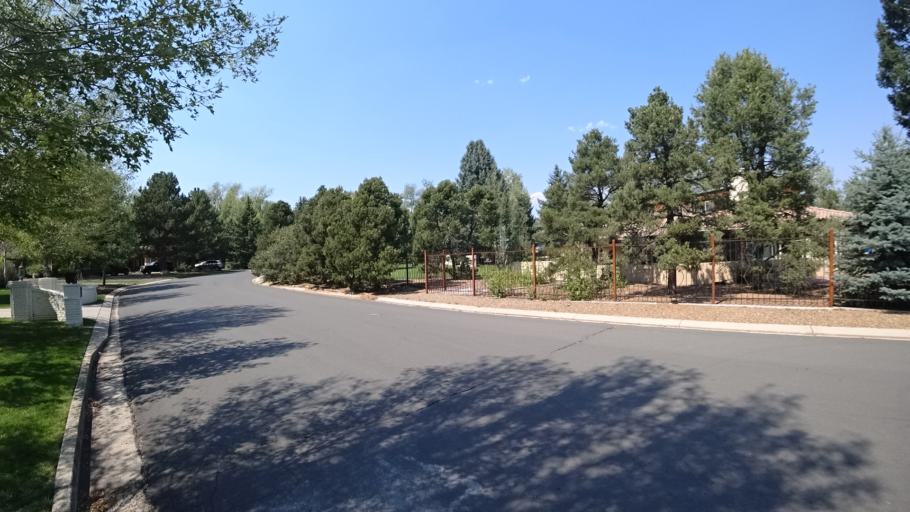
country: US
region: Colorado
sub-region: El Paso County
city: Colorado Springs
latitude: 38.7969
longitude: -104.8402
